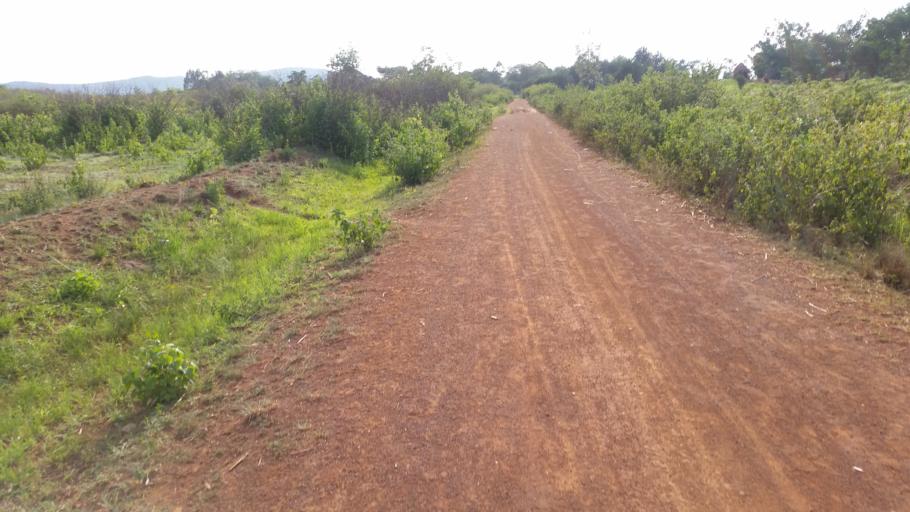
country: UG
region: Eastern Region
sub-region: Busia District
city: Busia
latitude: 0.5506
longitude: 33.9885
